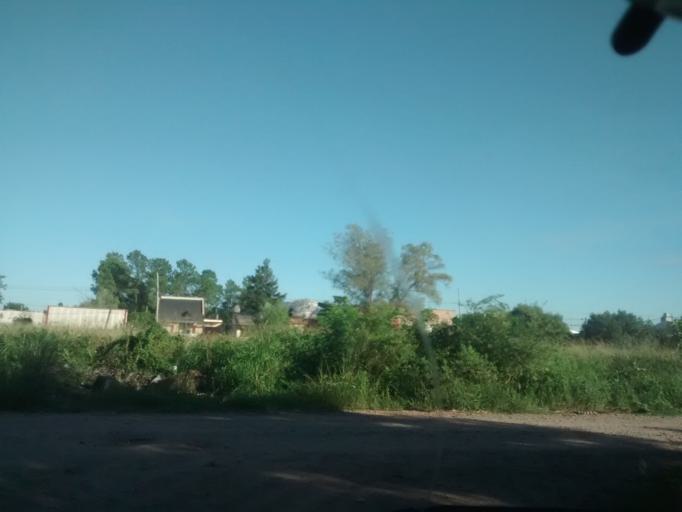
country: AR
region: Chaco
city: Fontana
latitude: -27.4561
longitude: -59.0302
